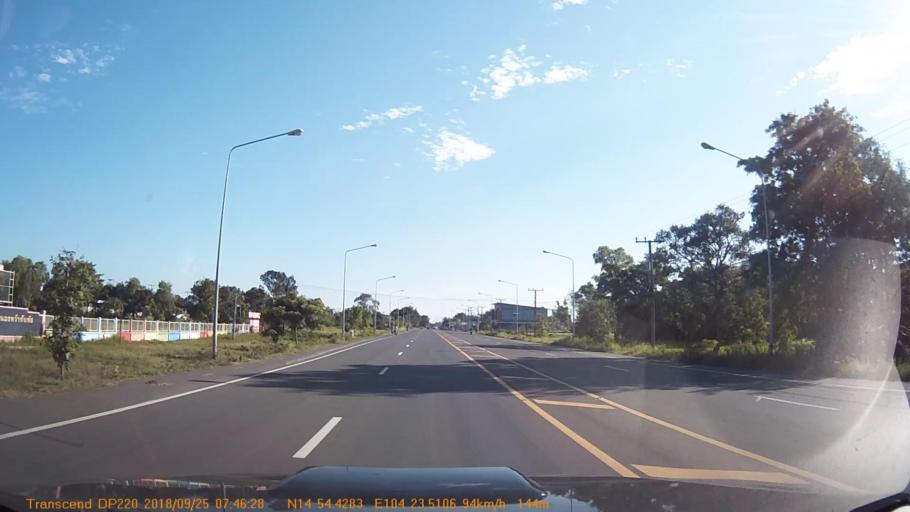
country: TH
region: Sisaket
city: Phayu
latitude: 14.9074
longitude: 104.3920
